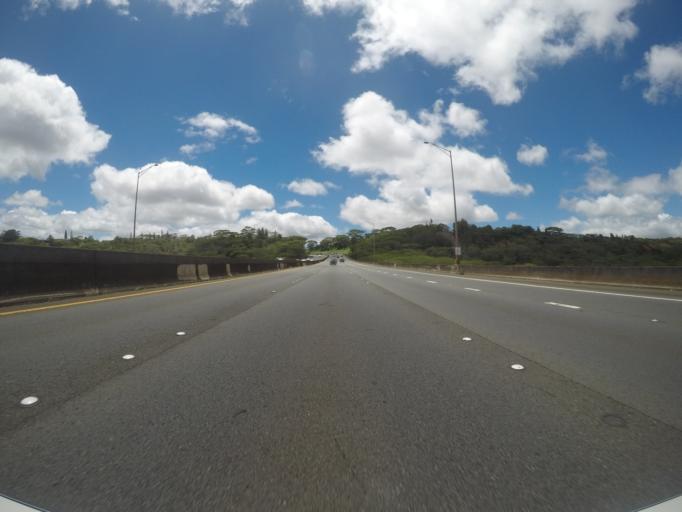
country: US
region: Hawaii
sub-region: Honolulu County
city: Mililani Town
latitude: 21.4584
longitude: -157.9928
